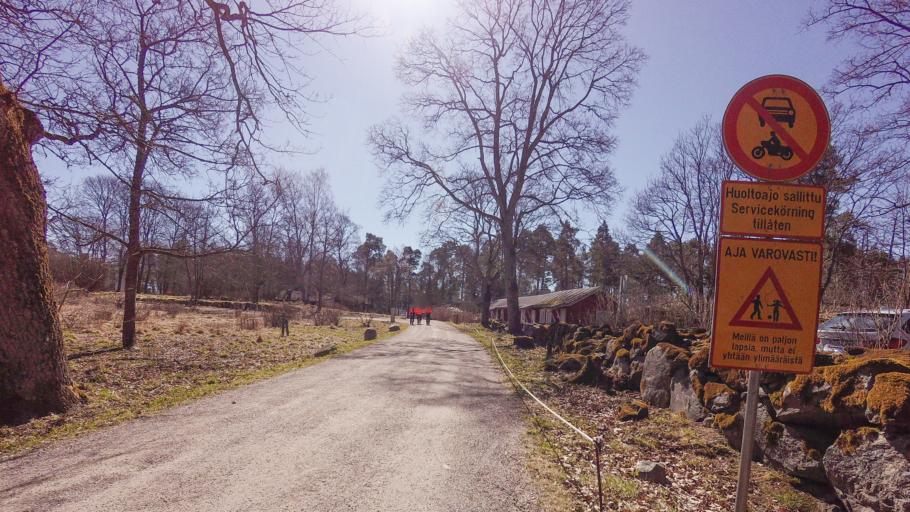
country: FI
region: Uusimaa
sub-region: Helsinki
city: Helsinki
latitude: 60.1642
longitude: 25.0286
